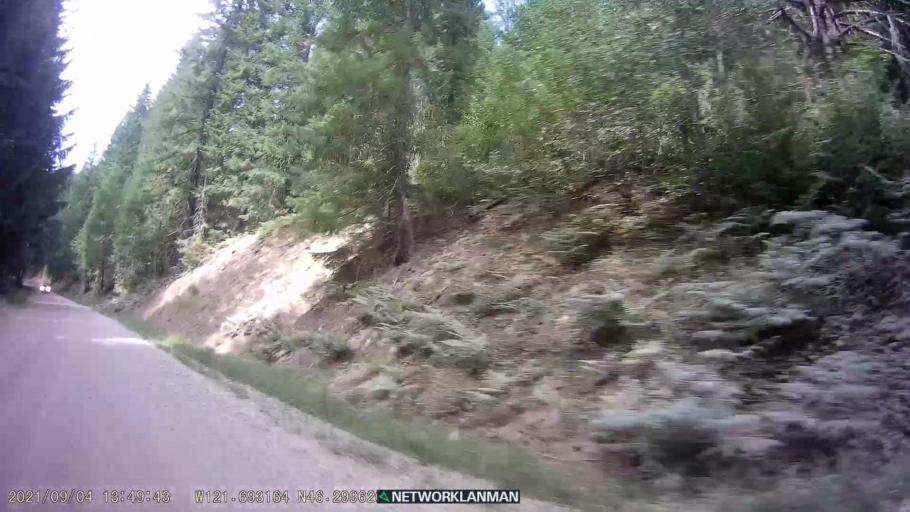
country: US
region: Washington
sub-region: Skamania County
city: Carson
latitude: 46.2996
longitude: -121.6934
